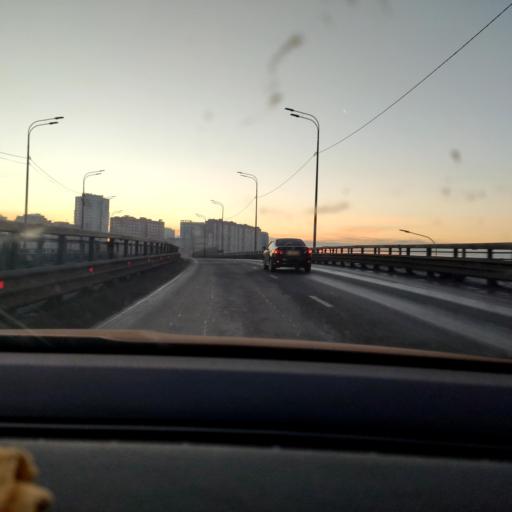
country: RU
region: Moskovskaya
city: Odintsovo
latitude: 55.6703
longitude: 37.2761
